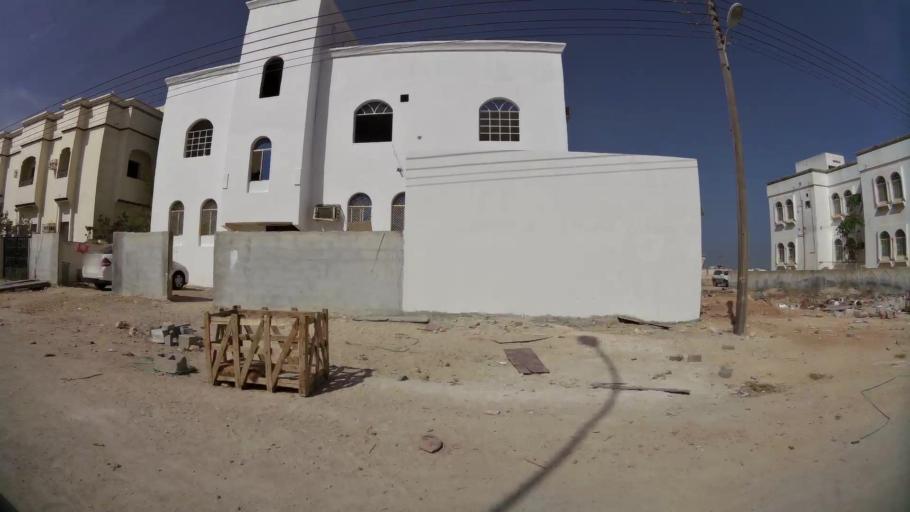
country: OM
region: Zufar
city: Salalah
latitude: 16.9986
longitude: 54.0130
